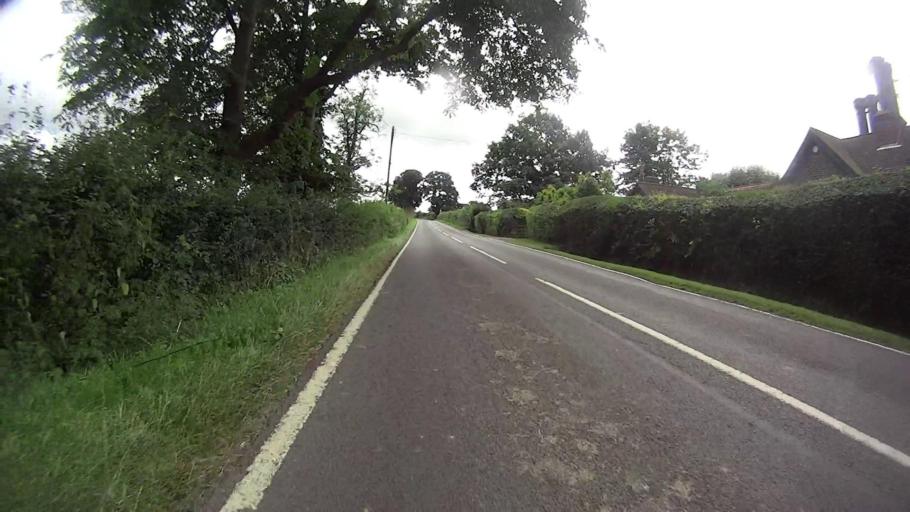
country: GB
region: England
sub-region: Surrey
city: Reigate
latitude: 51.1821
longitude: -0.2314
